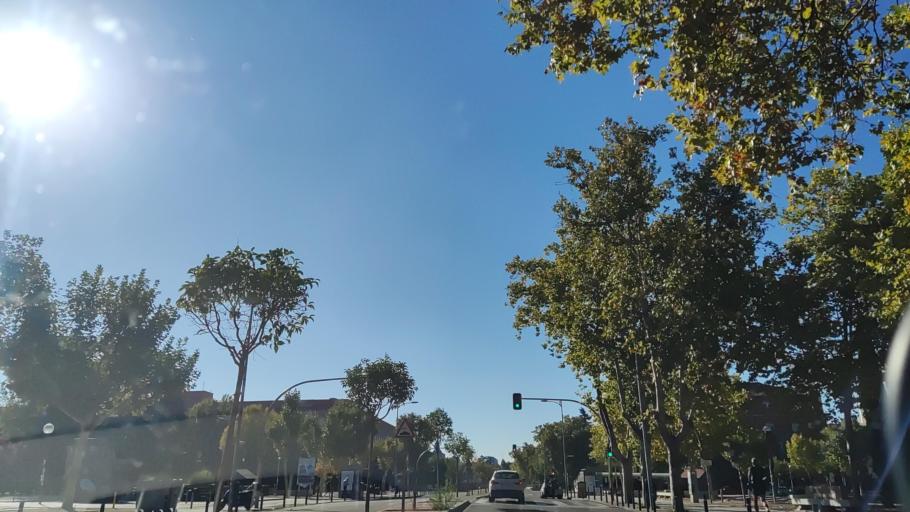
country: ES
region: Madrid
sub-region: Provincia de Madrid
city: Moncloa-Aravaca
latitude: 40.4441
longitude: -3.7274
